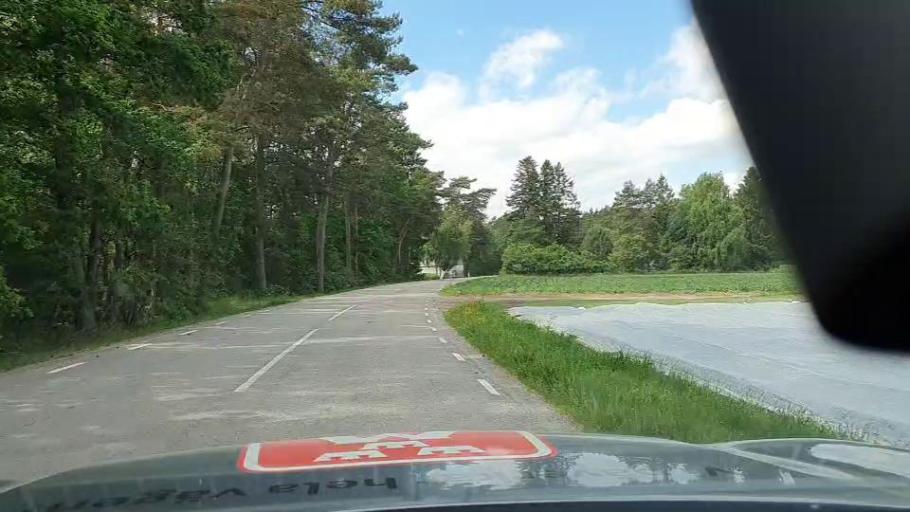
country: SE
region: Blekinge
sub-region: Karlshamns Kommun
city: Morrum
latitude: 56.0919
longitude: 14.6981
